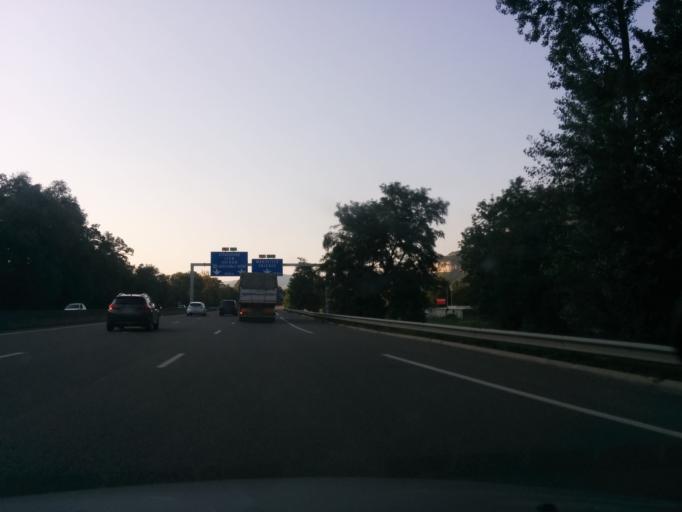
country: FR
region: Rhone-Alpes
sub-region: Departement de l'Isere
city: Veurey-Voroize
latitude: 45.2856
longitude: 5.6210
